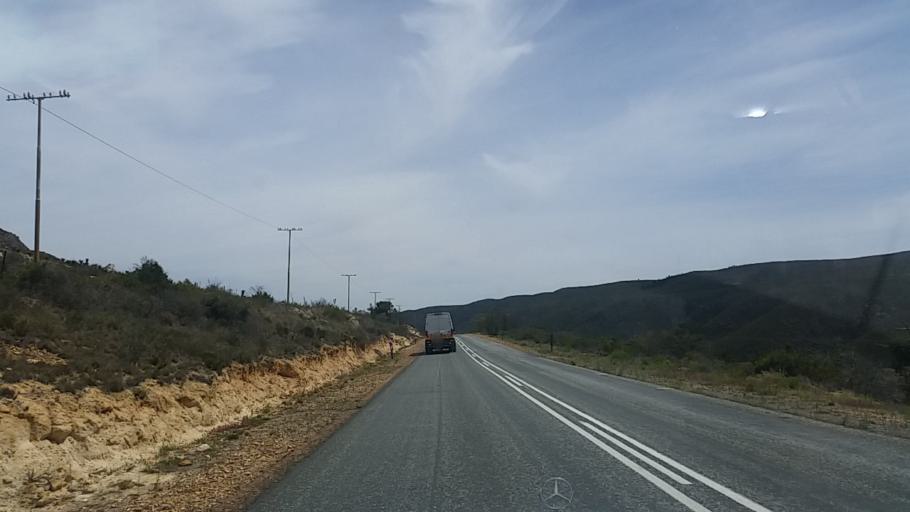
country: ZA
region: Western Cape
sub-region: Eden District Municipality
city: Knysna
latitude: -33.7423
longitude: 23.0282
